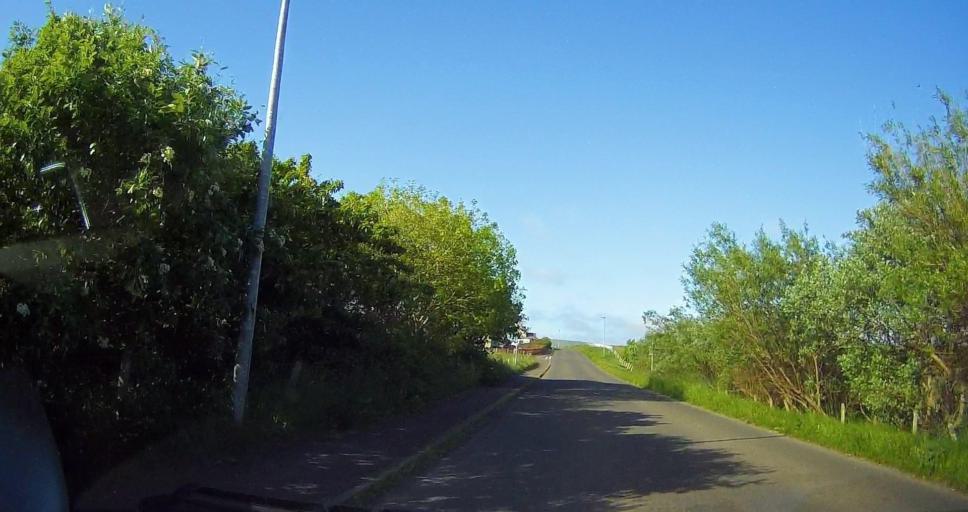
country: GB
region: Scotland
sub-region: Orkney Islands
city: Stromness
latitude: 59.0689
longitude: -3.2288
